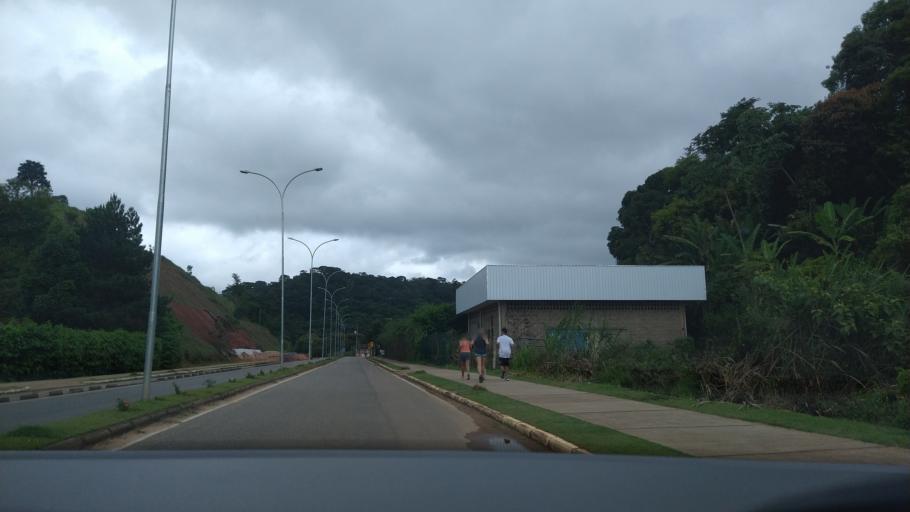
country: BR
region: Minas Gerais
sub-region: Vicosa
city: Vicosa
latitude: -20.7698
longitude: -42.8581
